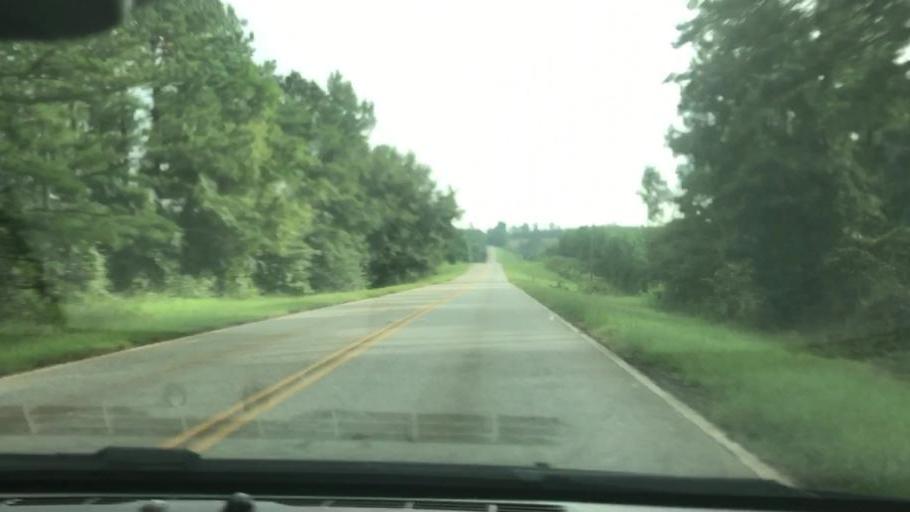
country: US
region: Georgia
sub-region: Quitman County
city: Georgetown
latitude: 31.9183
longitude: -85.0251
